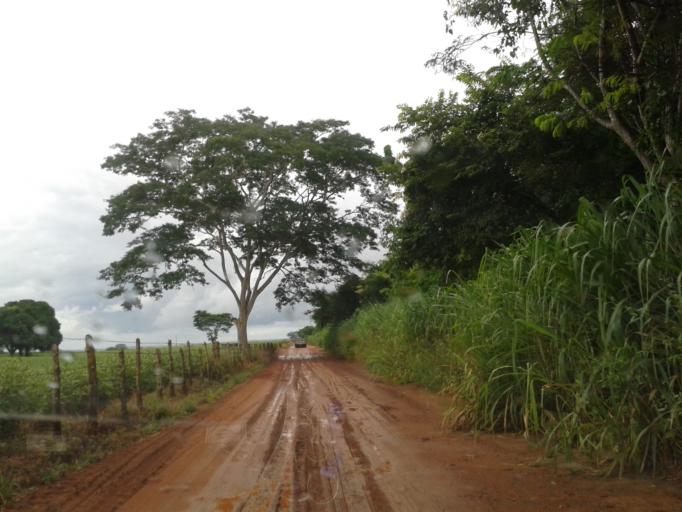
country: BR
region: Minas Gerais
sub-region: Santa Vitoria
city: Santa Vitoria
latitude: -18.7032
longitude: -49.9595
